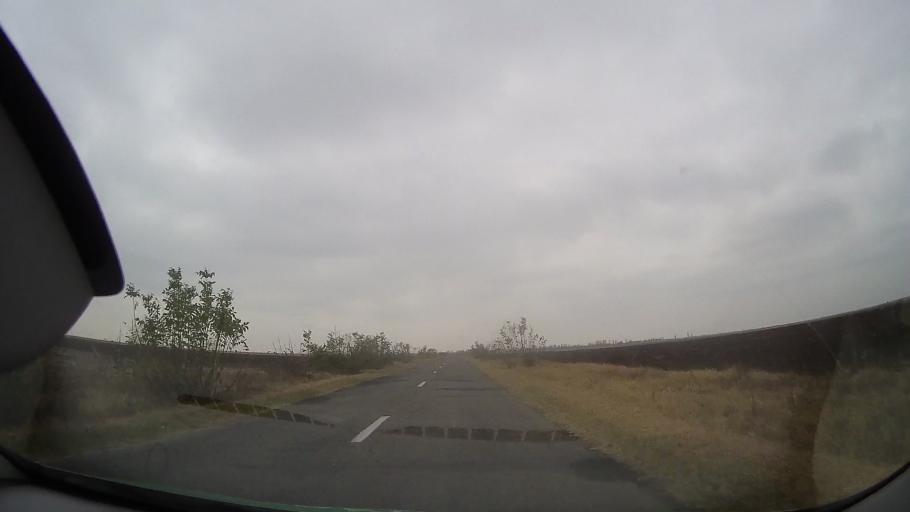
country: RO
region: Ialomita
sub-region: Comuna Valea Macrisului
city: Valea Macrisului
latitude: 44.7597
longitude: 26.8015
